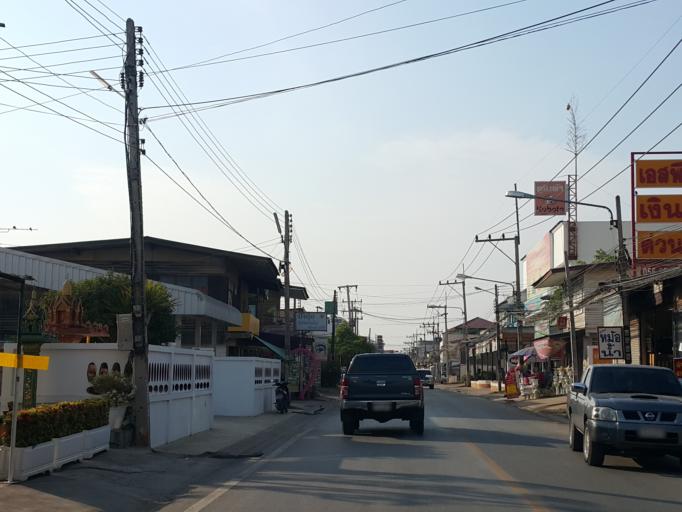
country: TH
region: Phitsanulok
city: Phrom Phiram
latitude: 17.0990
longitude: 100.1677
